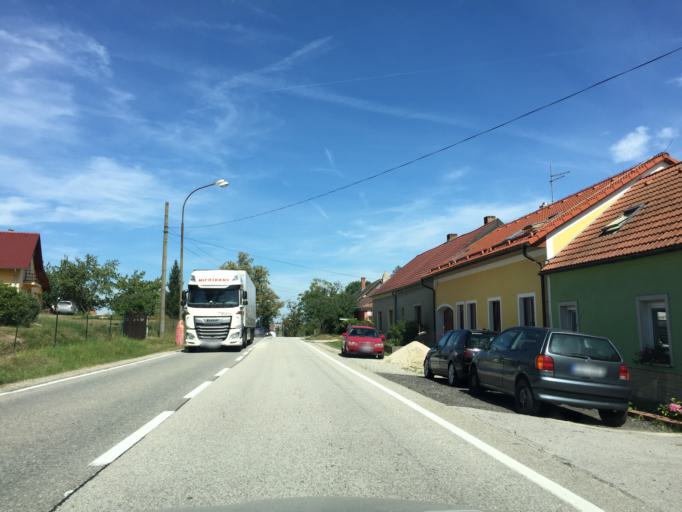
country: CZ
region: Jihocesky
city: Sevetin
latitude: 49.0910
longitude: 14.5519
